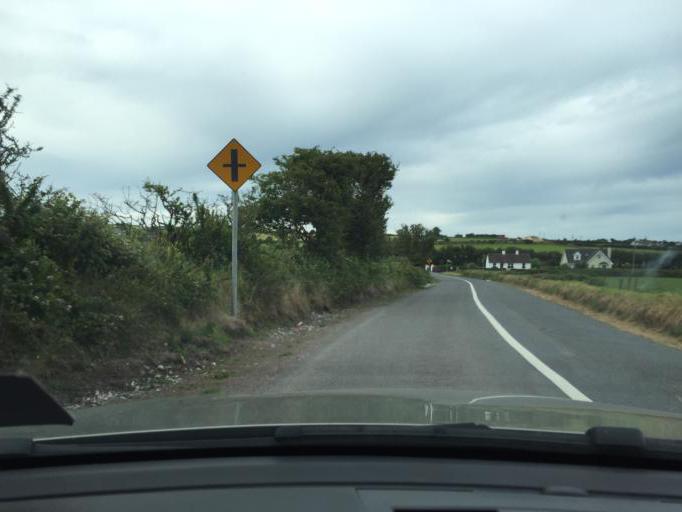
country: IE
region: Munster
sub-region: County Cork
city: Youghal
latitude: 51.9748
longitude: -7.7163
